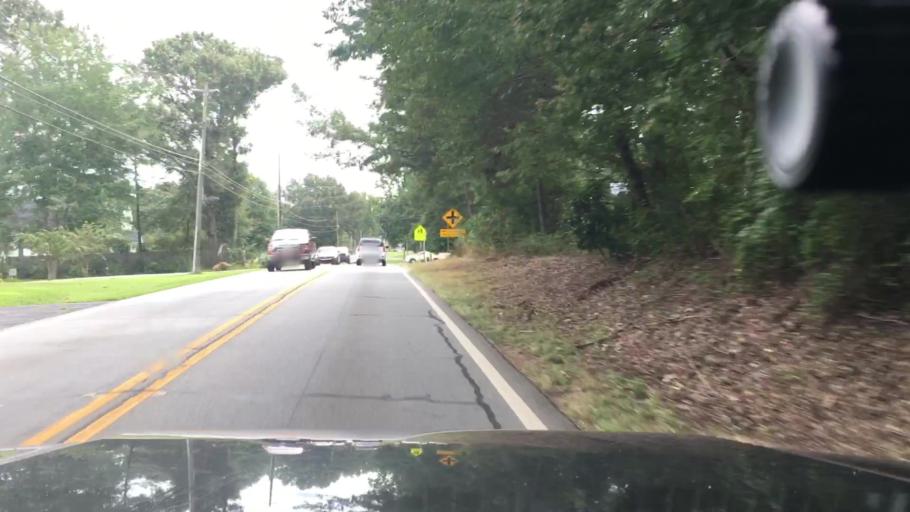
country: US
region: Georgia
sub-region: Coweta County
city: East Newnan
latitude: 33.2879
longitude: -84.7681
